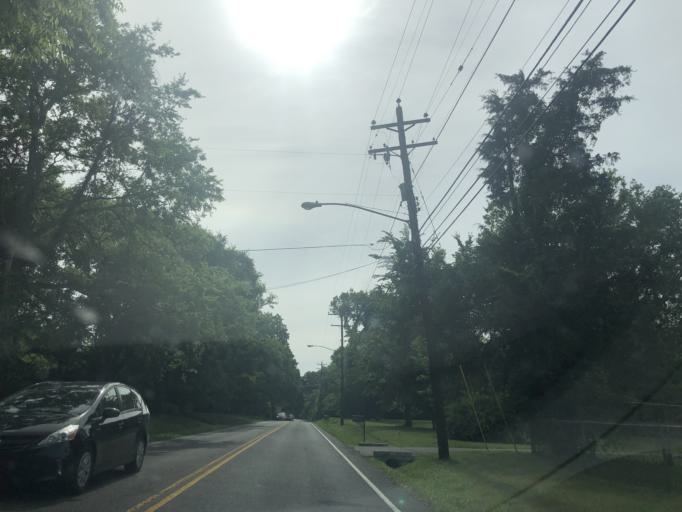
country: US
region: Tennessee
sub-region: Davidson County
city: Oak Hill
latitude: 36.0881
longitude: -86.7842
